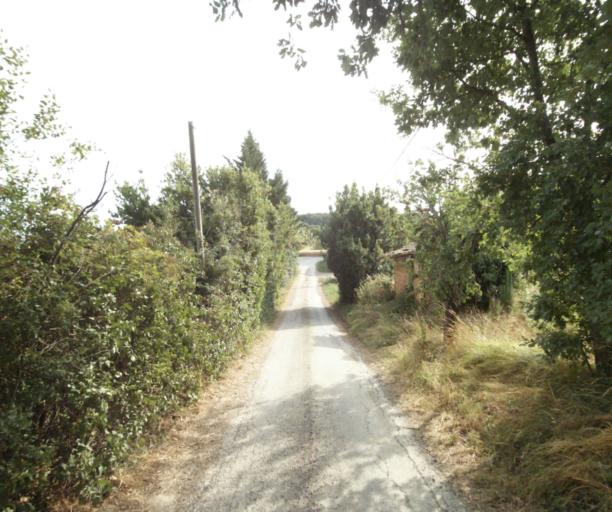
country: FR
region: Midi-Pyrenees
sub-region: Departement du Tarn
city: Puylaurens
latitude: 43.5334
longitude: 2.0551
